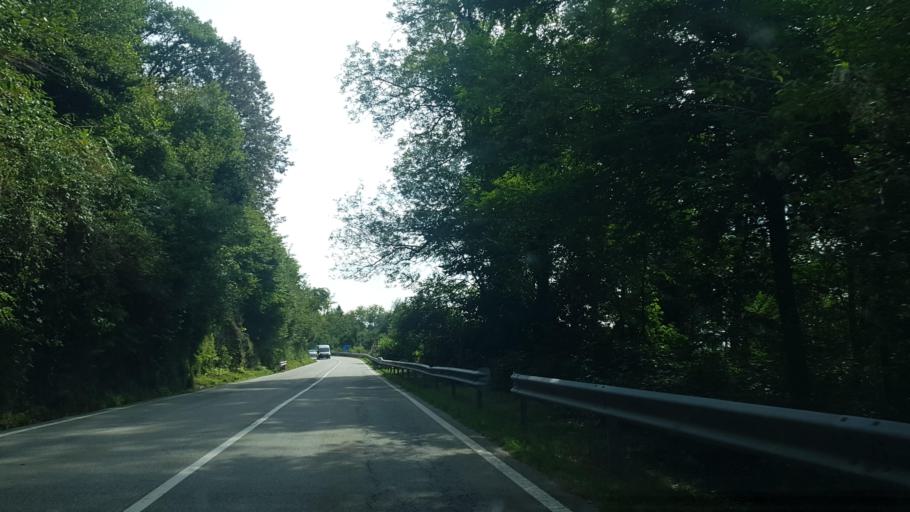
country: IT
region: Piedmont
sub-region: Provincia Verbano-Cusio-Ossola
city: Vignone
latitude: 45.9622
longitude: 8.5680
